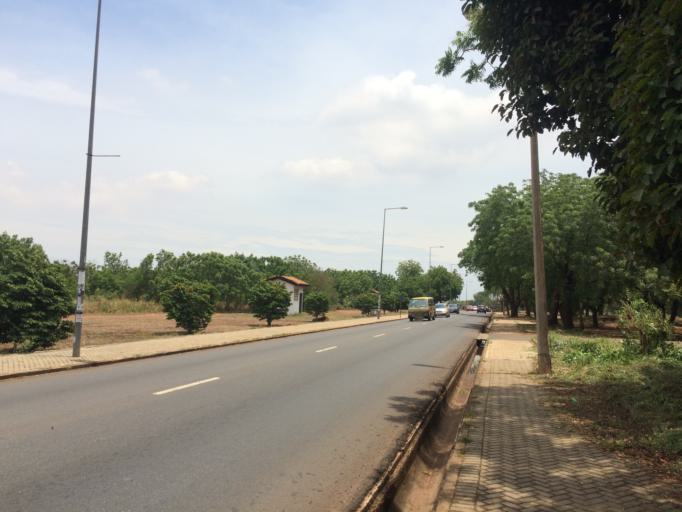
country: GH
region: Greater Accra
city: Medina Estates
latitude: 5.6424
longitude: -0.1844
